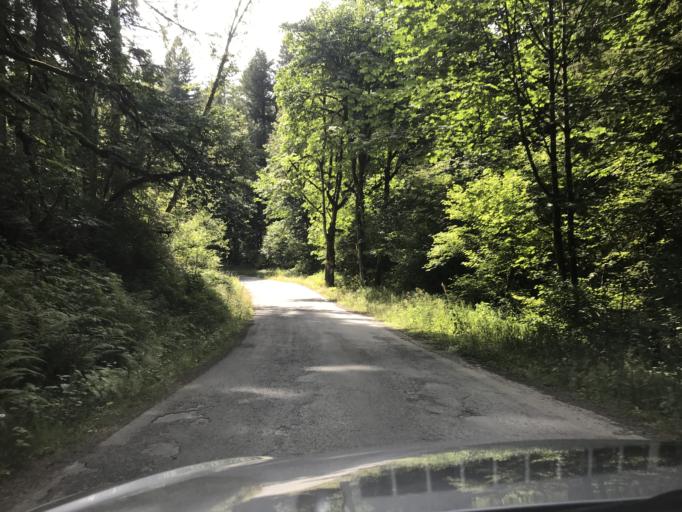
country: US
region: Washington
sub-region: King County
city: Hobart
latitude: 47.4165
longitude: -121.9187
